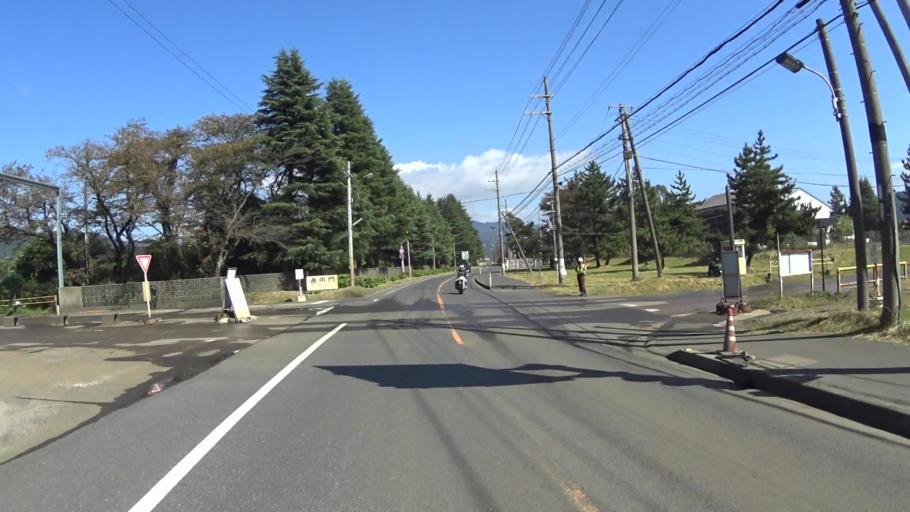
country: JP
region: Kyoto
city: Miyazu
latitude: 35.5555
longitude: 135.1513
